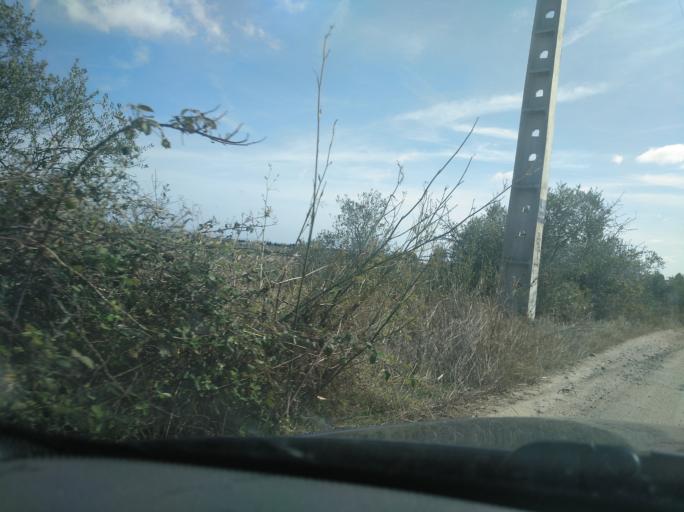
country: PT
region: Portalegre
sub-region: Campo Maior
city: Campo Maior
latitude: 39.0382
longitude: -7.0516
